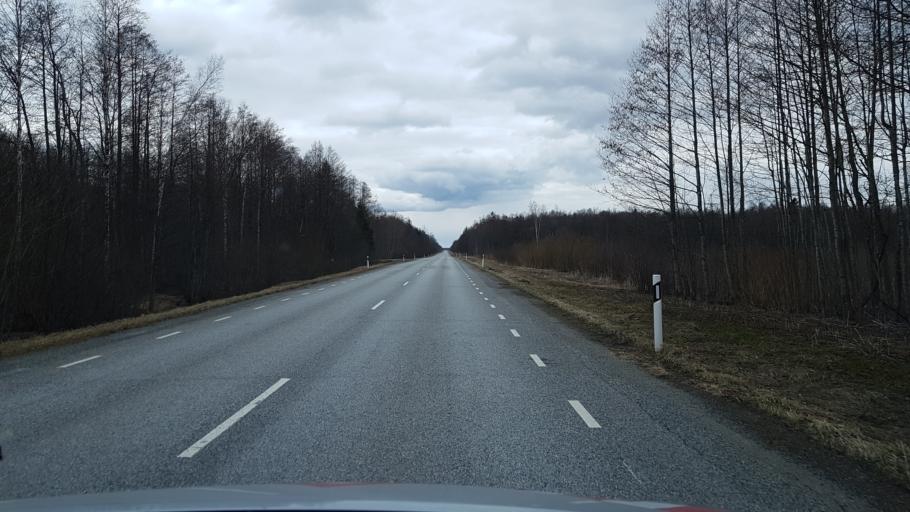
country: EE
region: Ida-Virumaa
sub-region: Narva-Joesuu linn
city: Narva-Joesuu
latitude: 59.3430
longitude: 27.9950
